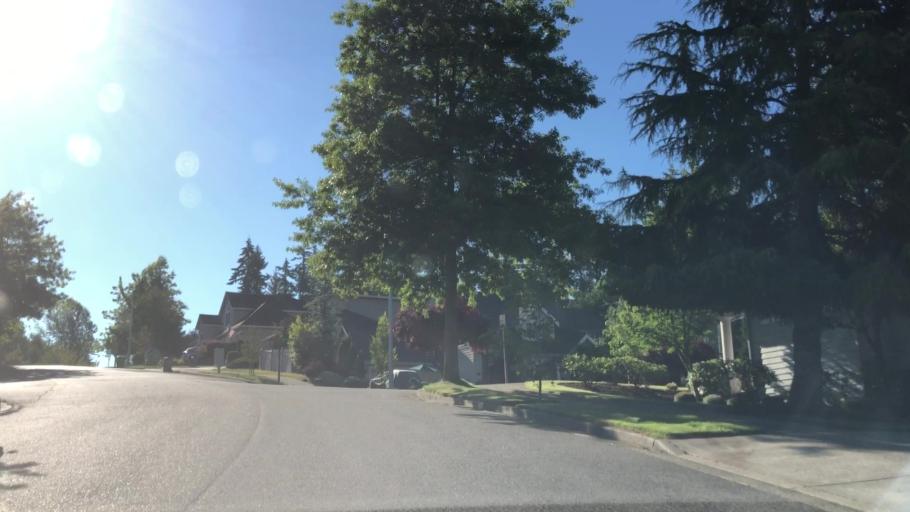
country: US
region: Washington
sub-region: Snohomish County
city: North Creek
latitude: 47.8138
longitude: -122.1956
